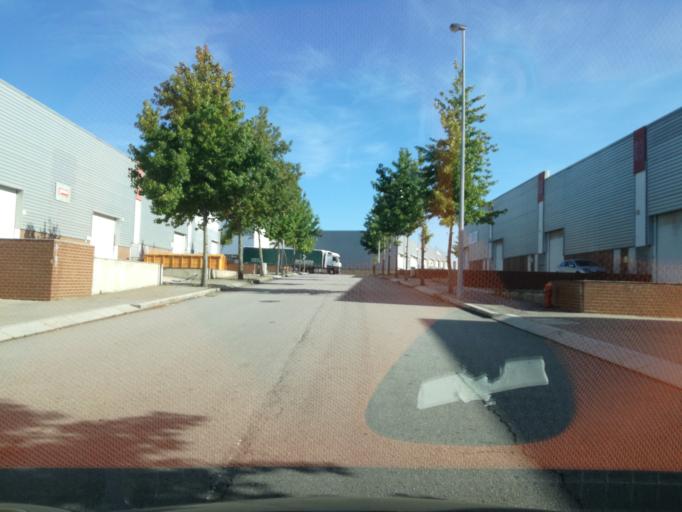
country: PT
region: Porto
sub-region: Maia
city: Anta
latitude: 41.2756
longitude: -8.6050
